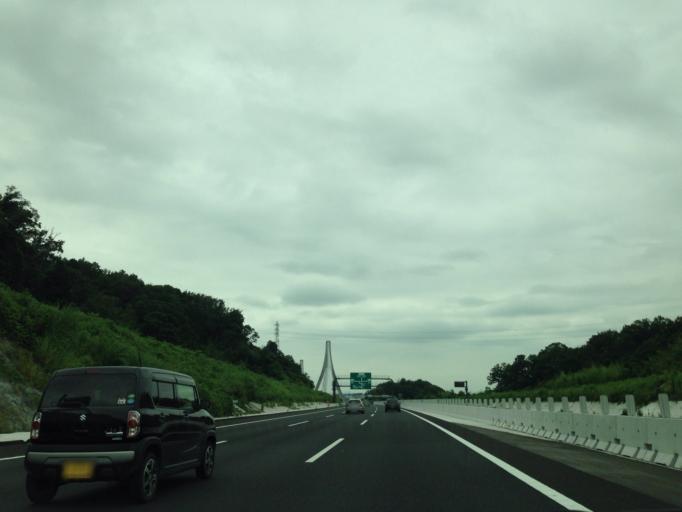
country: JP
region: Aichi
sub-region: Toyota-shi
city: Toyota
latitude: 35.0436
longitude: 137.1876
